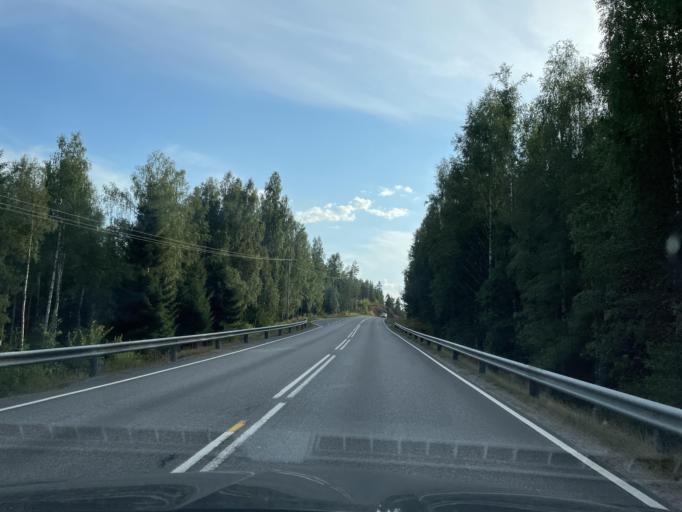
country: FI
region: Paijanne Tavastia
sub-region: Lahti
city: Auttoinen
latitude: 61.3196
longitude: 25.1416
